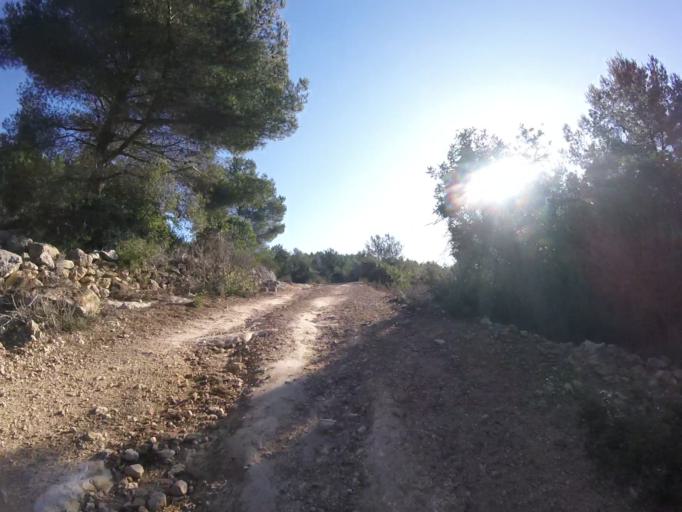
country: ES
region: Valencia
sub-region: Provincia de Castello
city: Torreblanca
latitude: 40.2532
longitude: 0.1883
